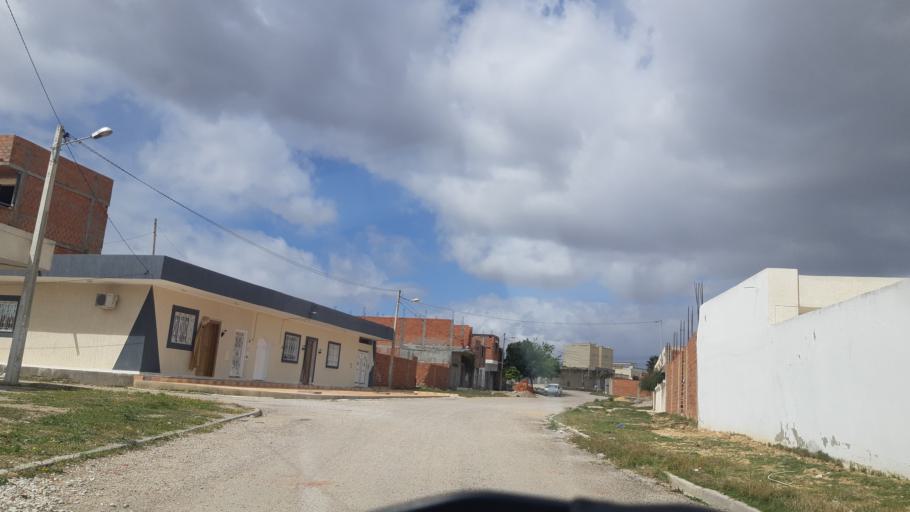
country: TN
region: Susah
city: Akouda
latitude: 35.8600
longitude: 10.5356
